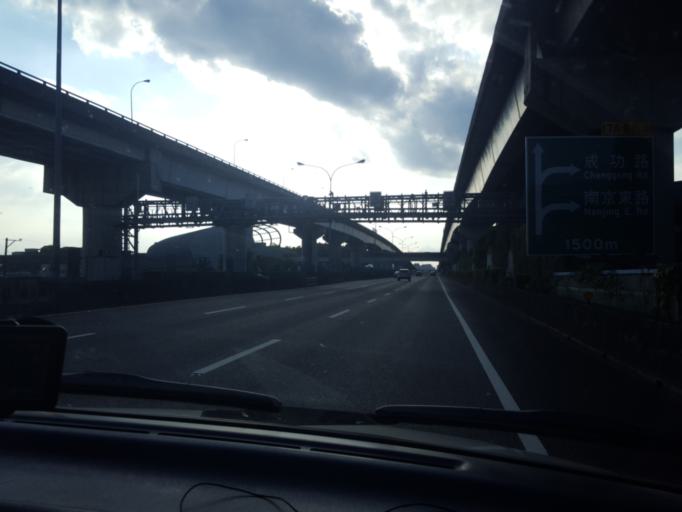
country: TW
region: Taipei
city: Taipei
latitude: 25.0658
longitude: 121.6141
